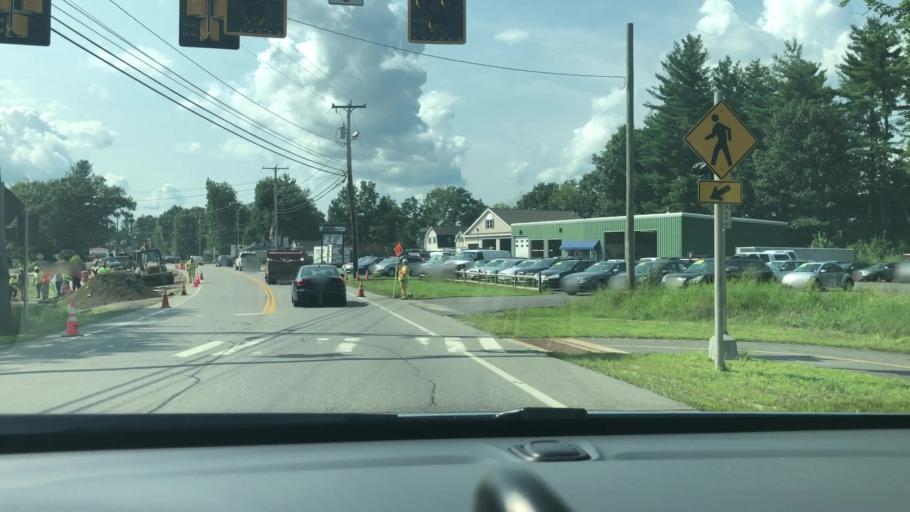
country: US
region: New Hampshire
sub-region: Hillsborough County
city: Pinardville
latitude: 43.0115
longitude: -71.5468
